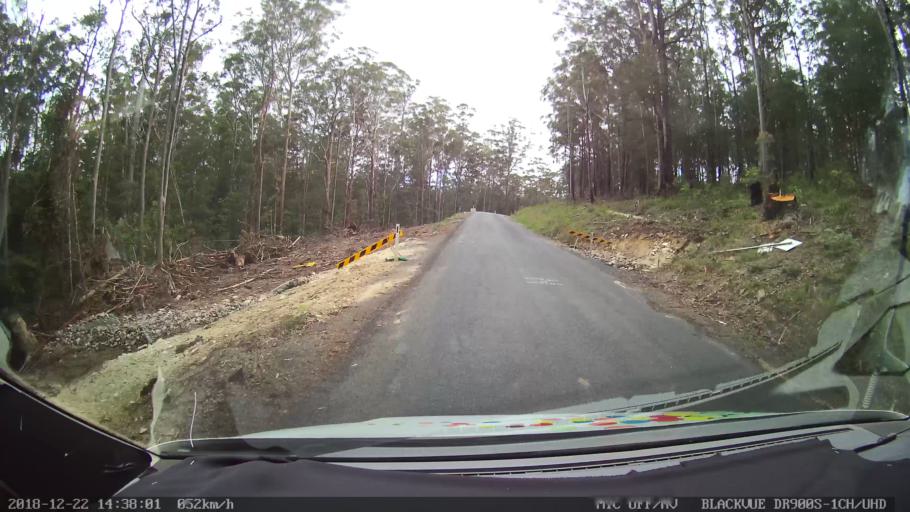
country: AU
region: New South Wales
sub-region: Bellingen
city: Dorrigo
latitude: -30.1360
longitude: 152.5997
